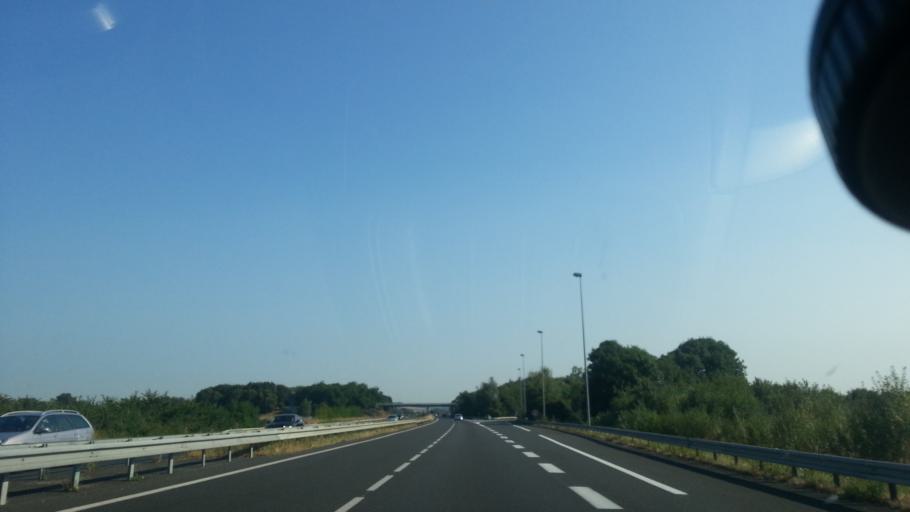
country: FR
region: Poitou-Charentes
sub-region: Departement de la Vienne
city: Antran
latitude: 46.8344
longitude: 0.5239
